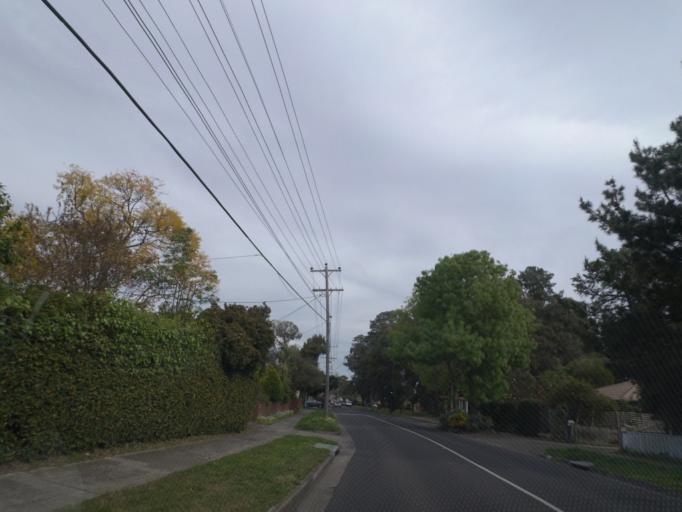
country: AU
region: Victoria
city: Forest Hill
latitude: -37.8262
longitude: 145.1856
